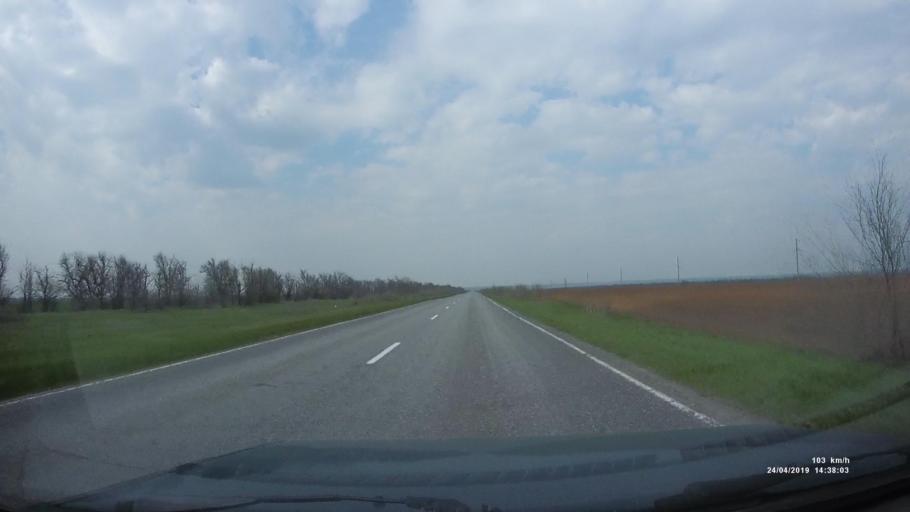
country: RU
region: Rostov
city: Remontnoye
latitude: 46.3954
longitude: 43.8861
